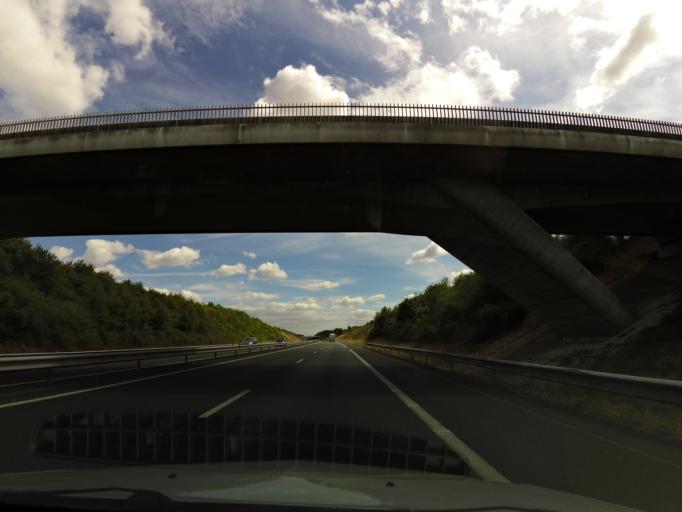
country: FR
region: Pays de la Loire
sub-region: Departement de la Vendee
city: Les Brouzils
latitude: 46.9117
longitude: -1.3228
